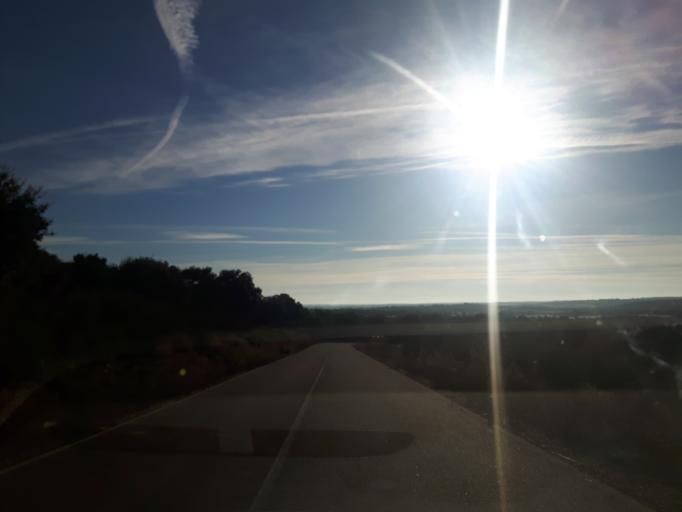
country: ES
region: Castille and Leon
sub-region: Provincia de Salamanca
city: Olmedo de Camaces
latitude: 40.8966
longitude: -6.6213
